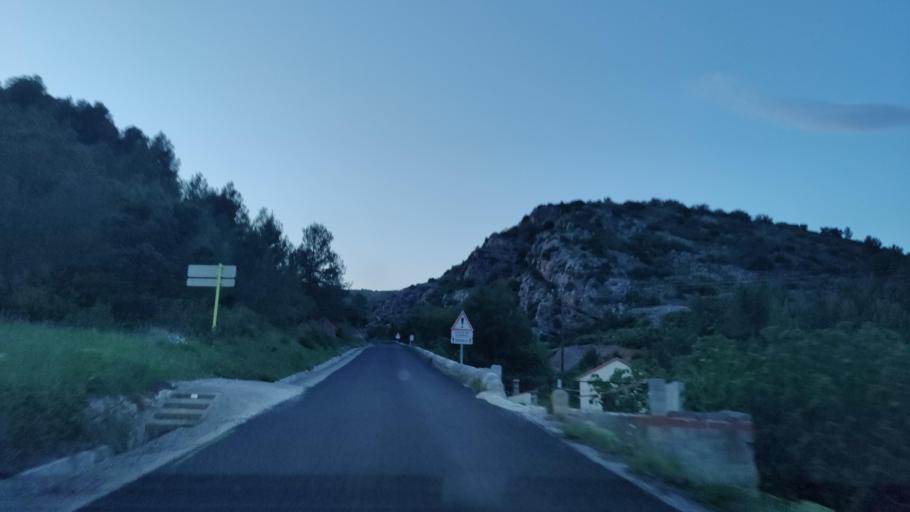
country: FR
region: Languedoc-Roussillon
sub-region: Departement des Pyrenees-Orientales
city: Baixas
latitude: 42.8519
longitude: 2.7728
